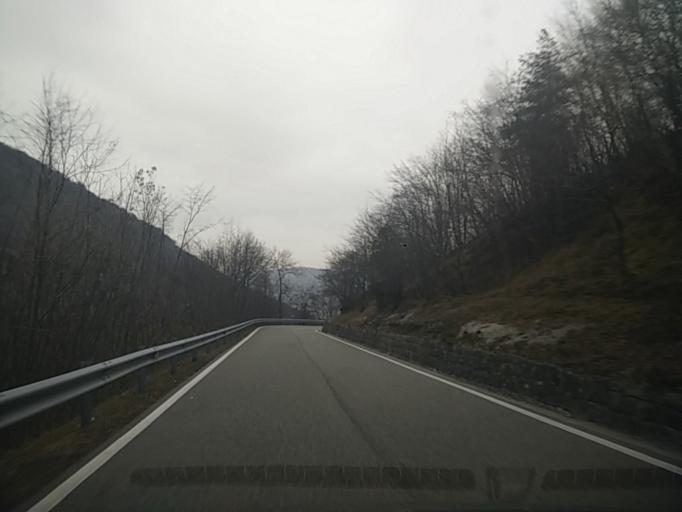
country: IT
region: Veneto
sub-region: Provincia di Treviso
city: Cison di Valmarino
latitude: 45.9932
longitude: 12.1729
